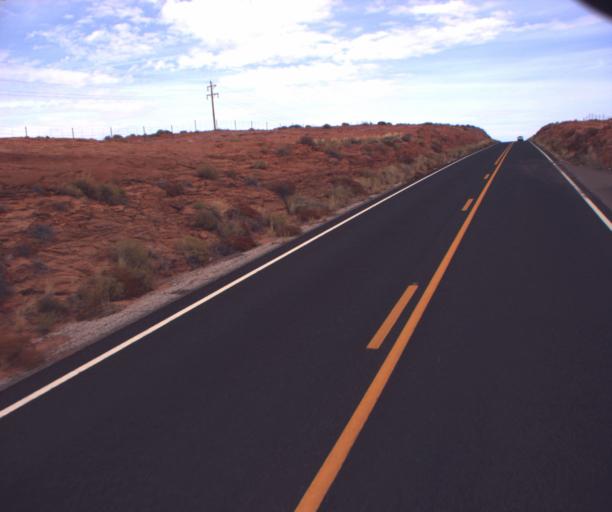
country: US
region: Arizona
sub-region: Apache County
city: Many Farms
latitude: 36.7876
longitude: -109.6536
